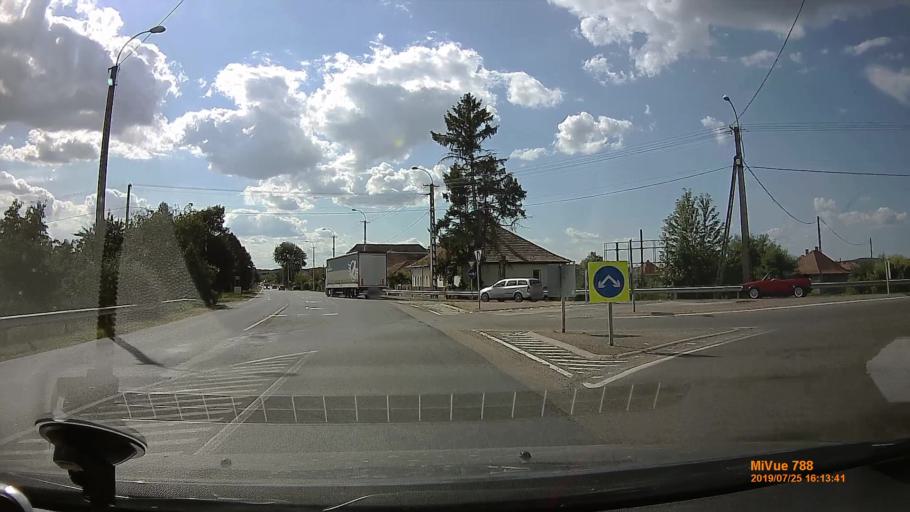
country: HU
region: Heves
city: Kerecsend
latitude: 47.7936
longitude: 20.3373
